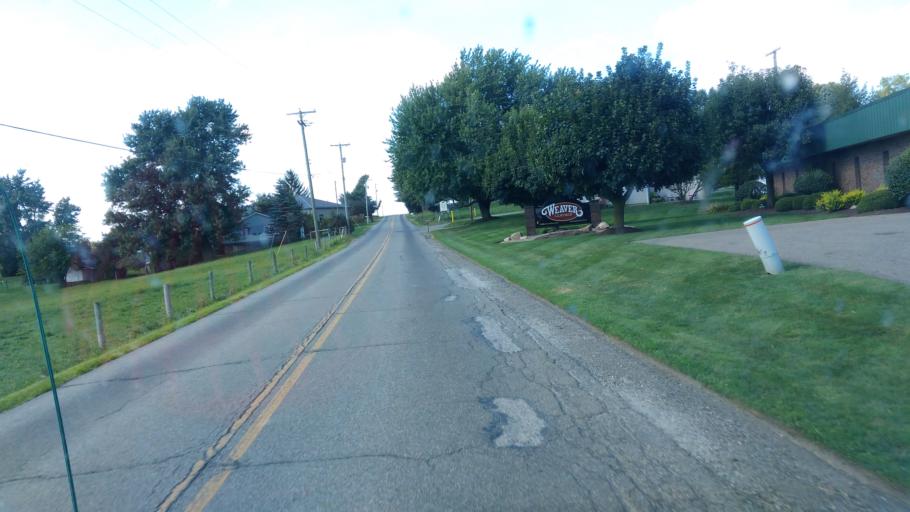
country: US
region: Ohio
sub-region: Holmes County
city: Millersburg
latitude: 40.6169
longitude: -81.8262
